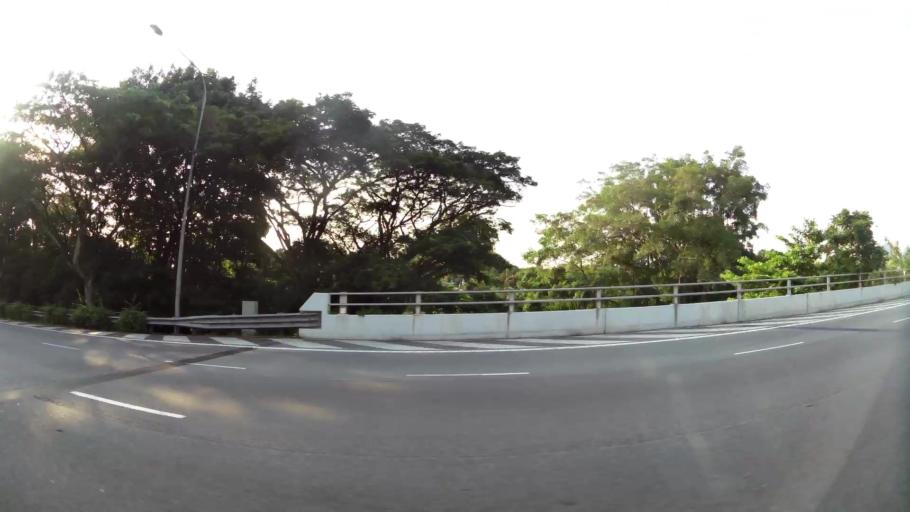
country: SG
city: Singapore
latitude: 1.2951
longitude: 103.8705
